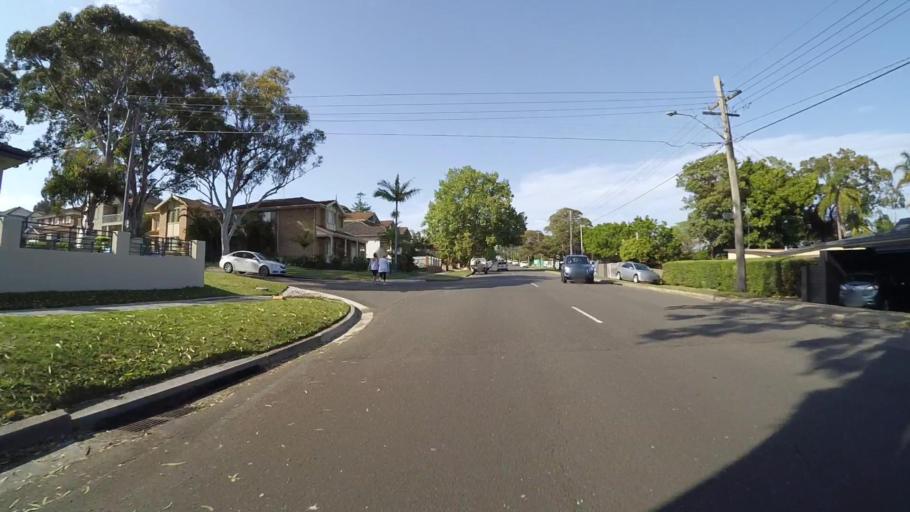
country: AU
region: New South Wales
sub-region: Sutherland Shire
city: Cronulla
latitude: -34.0575
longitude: 151.1395
